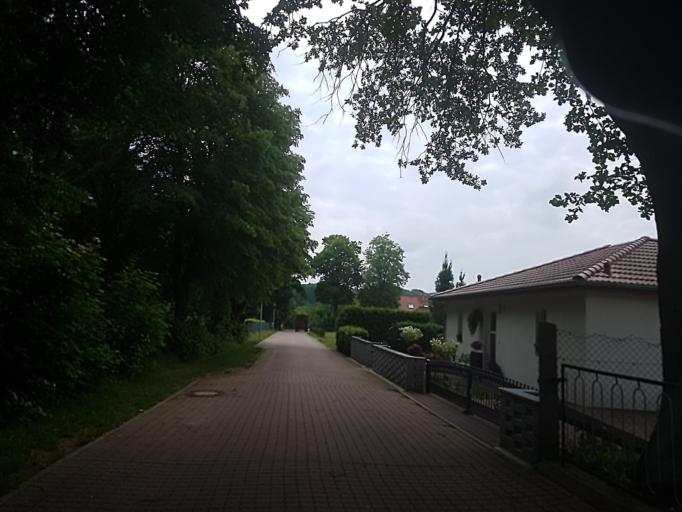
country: DE
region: Saxony-Anhalt
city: Lindau
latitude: 52.0800
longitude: 12.2457
